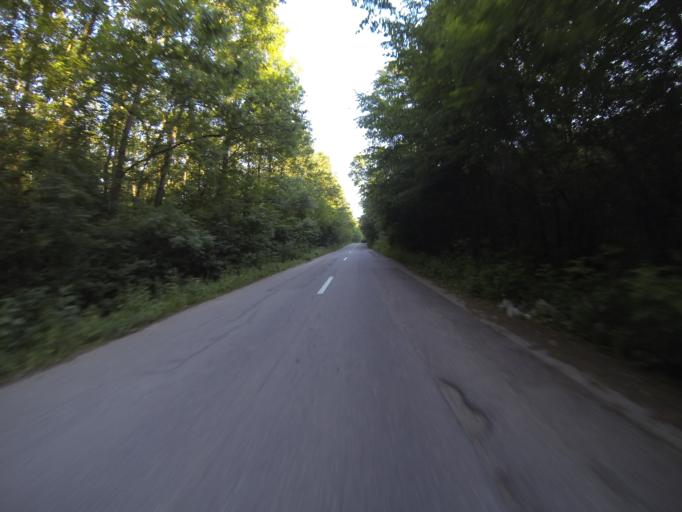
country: RO
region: Dolj
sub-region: Comuna Tuglui
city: Tuglui
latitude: 44.1673
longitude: 23.8258
